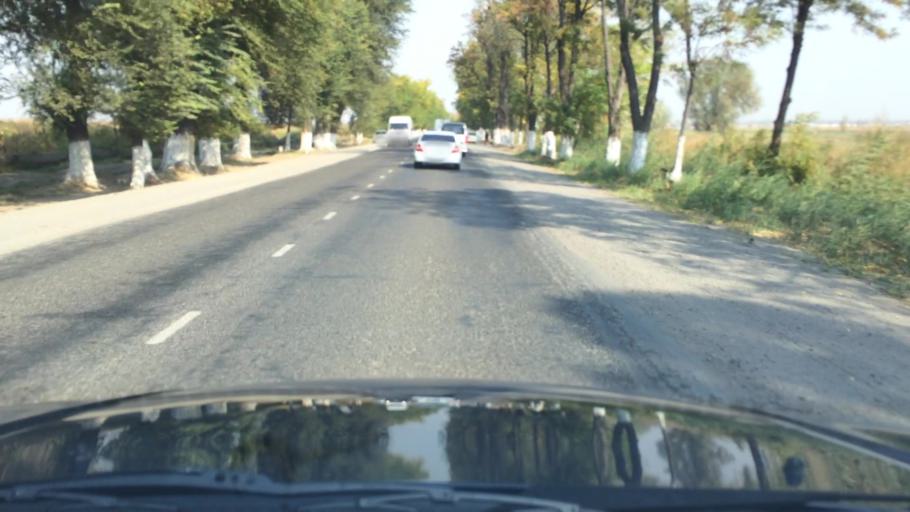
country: KG
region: Chuy
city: Lebedinovka
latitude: 42.9034
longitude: 74.6858
